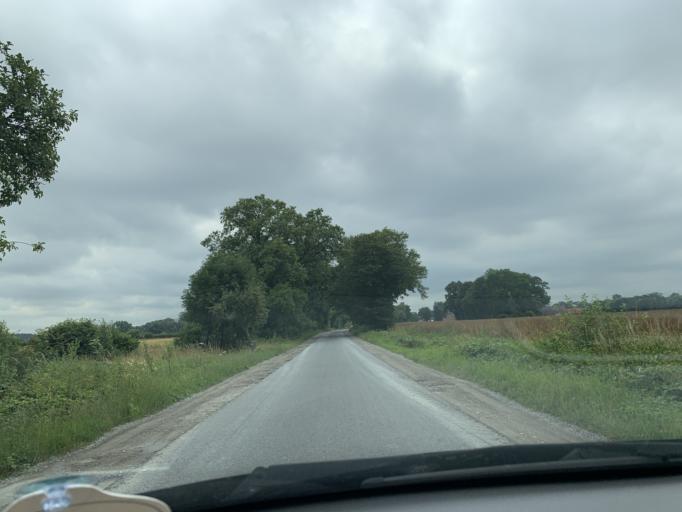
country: DE
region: North Rhine-Westphalia
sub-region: Regierungsbezirk Munster
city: Ennigerloh
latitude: 51.8353
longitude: 8.0754
